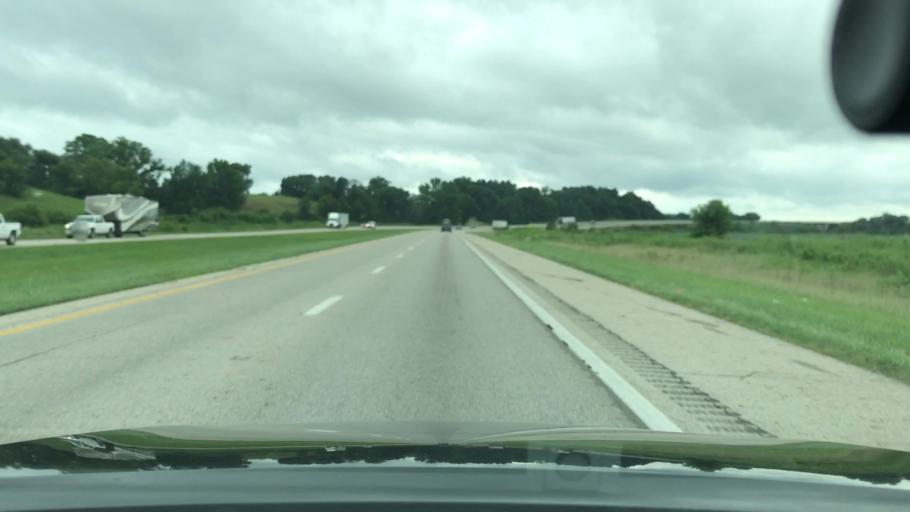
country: US
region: Ohio
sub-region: Ross County
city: Chillicothe
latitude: 39.2830
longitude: -82.8874
